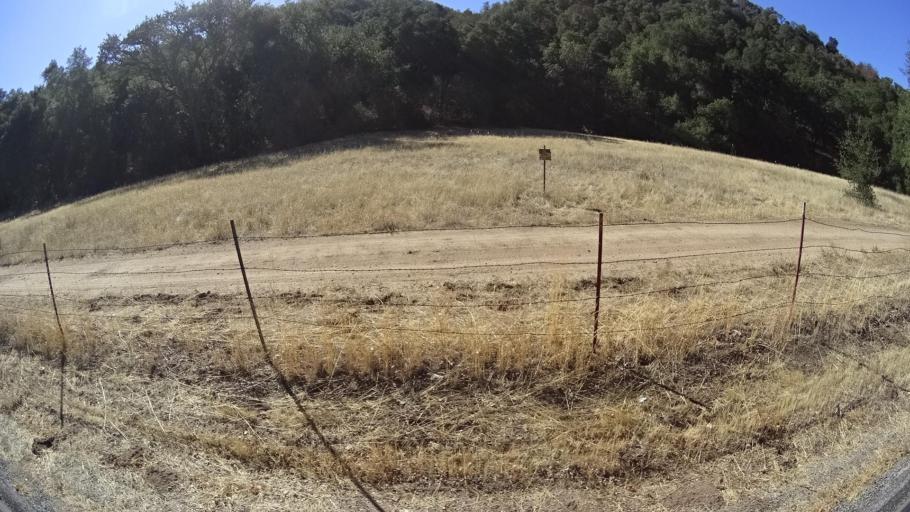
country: US
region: California
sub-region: Monterey County
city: Gonzales
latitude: 36.3790
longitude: -121.5659
